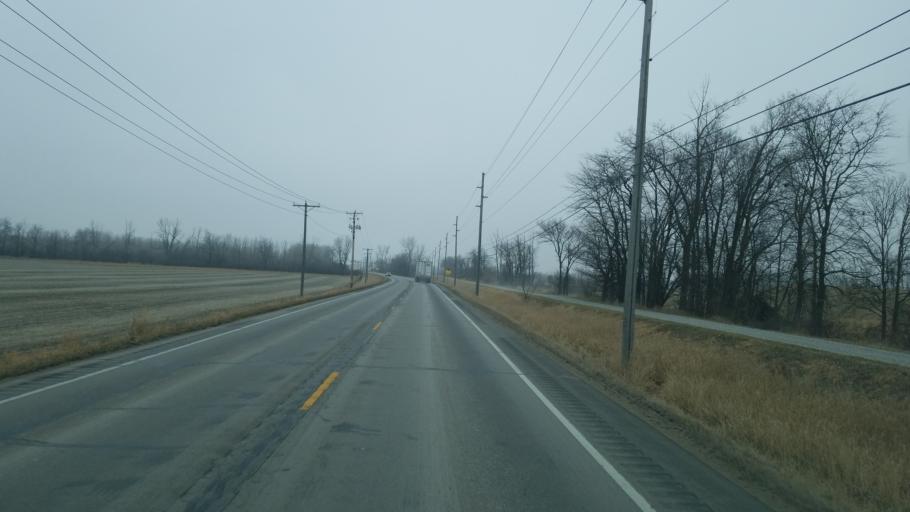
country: US
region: Indiana
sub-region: Adams County
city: Geneva
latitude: 40.5742
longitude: -84.9587
